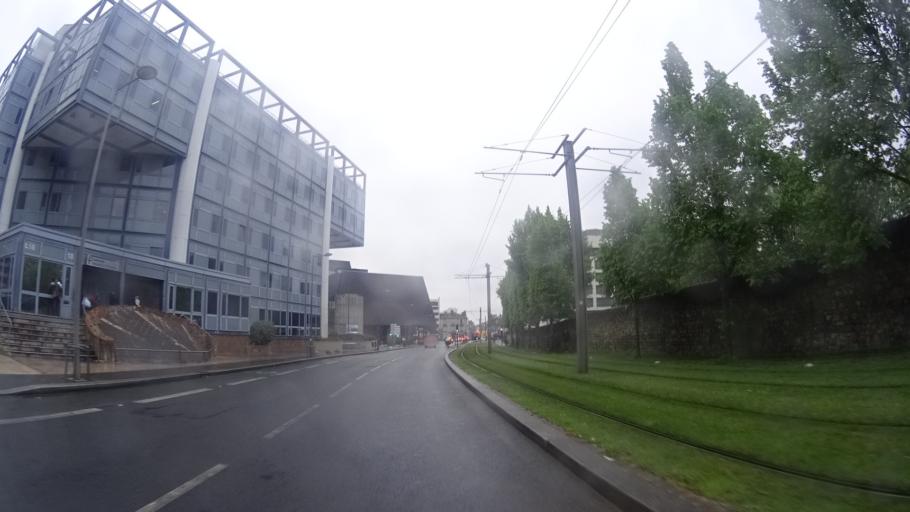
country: FR
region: Aquitaine
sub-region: Departement de la Gironde
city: Bordeaux
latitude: 44.8364
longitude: -0.5891
